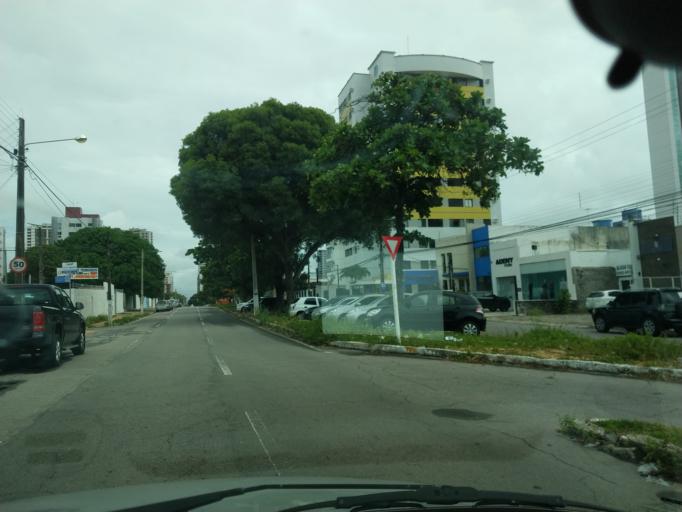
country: BR
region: Rio Grande do Norte
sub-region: Natal
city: Natal
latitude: -5.8154
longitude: -35.2148
